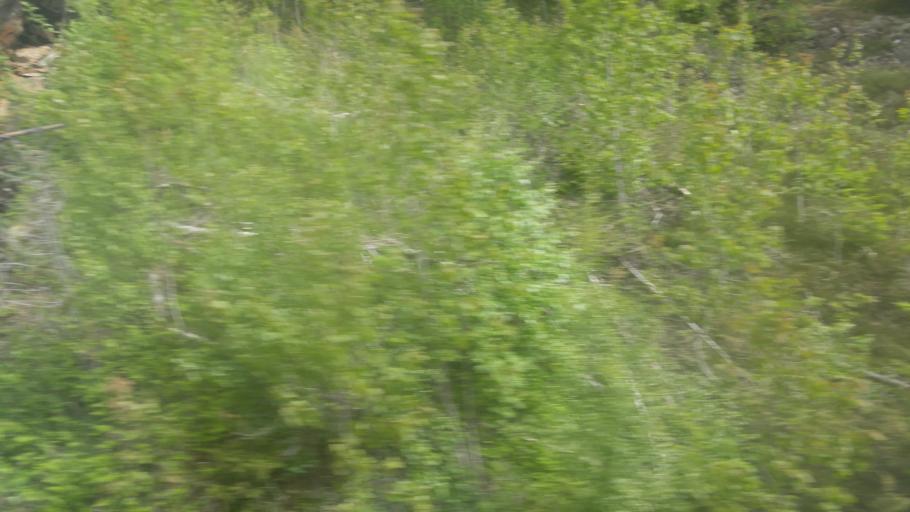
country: NO
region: Sor-Trondelag
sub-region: Selbu
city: Mebonden
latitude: 62.9646
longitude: 10.9679
